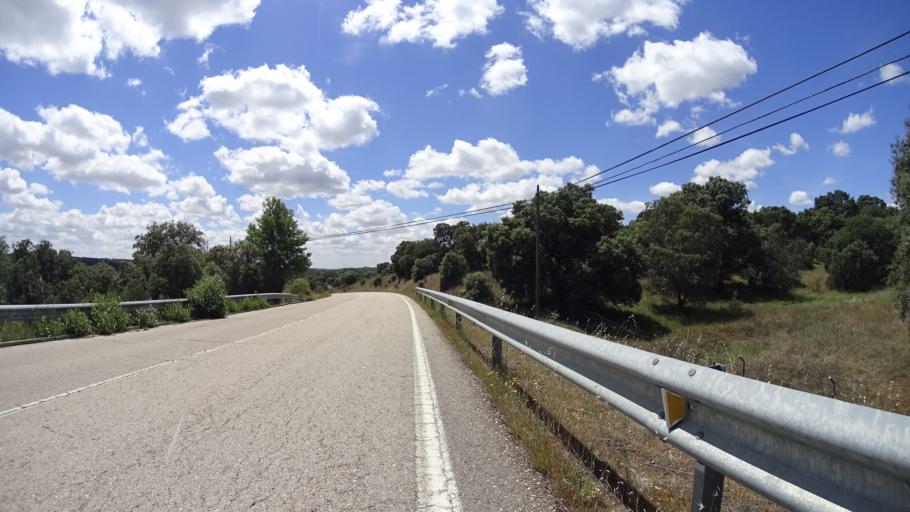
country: ES
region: Madrid
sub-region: Provincia de Madrid
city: Villanueva del Pardillo
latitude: 40.4476
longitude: -3.9537
